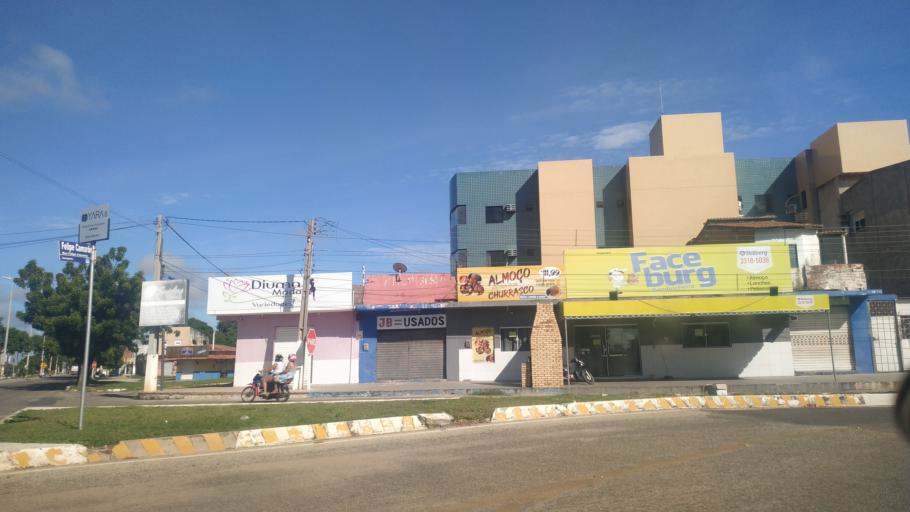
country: BR
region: Rio Grande do Norte
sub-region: Mossoro
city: Mossoro
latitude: -5.1921
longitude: -37.3668
